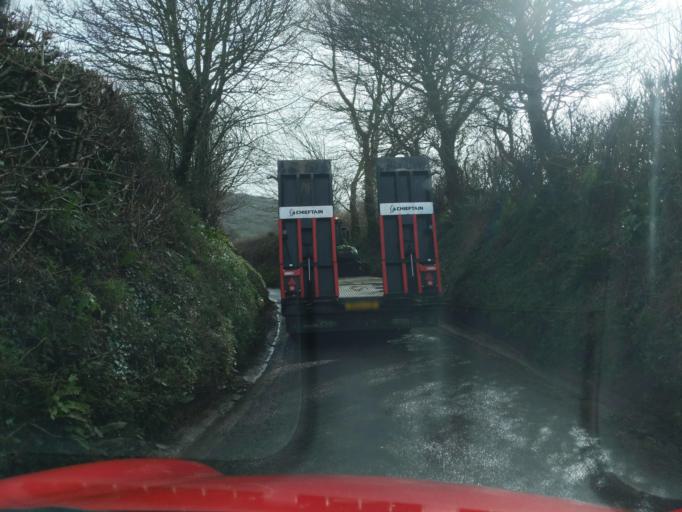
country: GB
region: England
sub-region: Devon
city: Ivybridge
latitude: 50.3548
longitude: -3.9294
